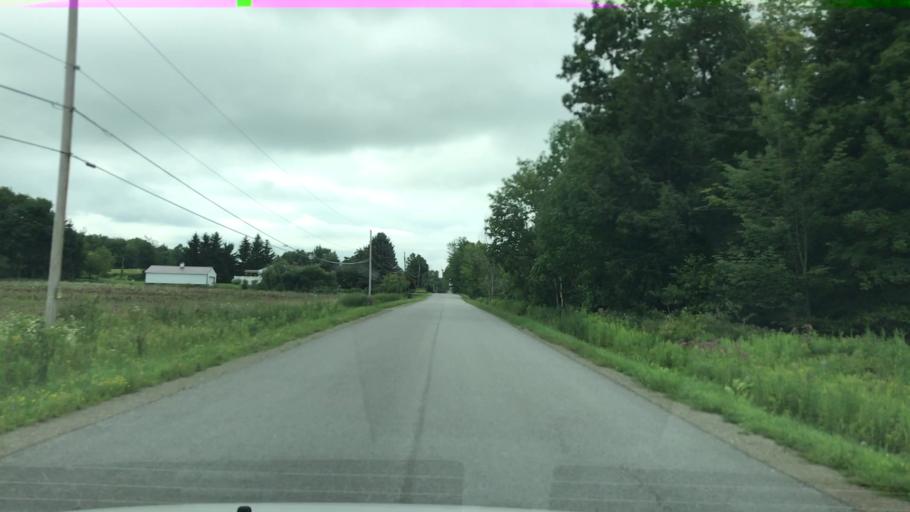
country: US
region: New York
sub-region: Wyoming County
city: Attica
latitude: 42.8256
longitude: -78.3362
